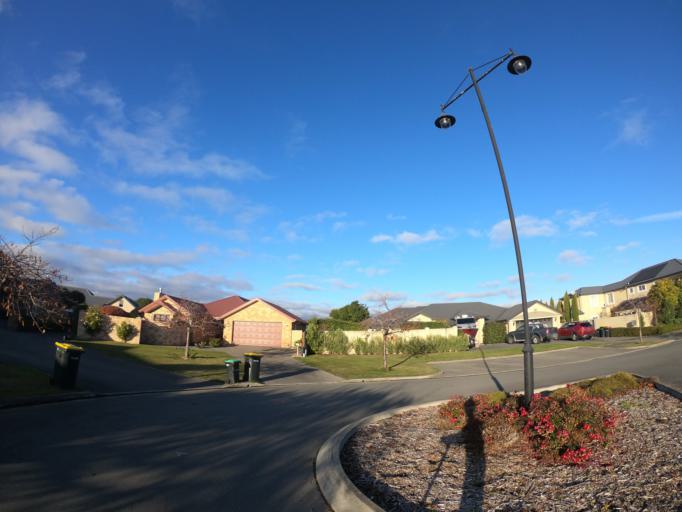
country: NZ
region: Canterbury
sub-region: Selwyn District
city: Prebbleton
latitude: -43.5664
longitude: 172.5660
